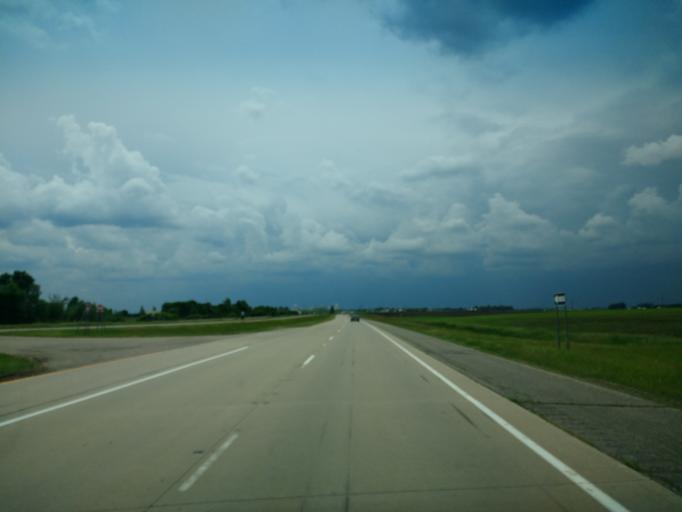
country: US
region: Minnesota
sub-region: Nobles County
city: Worthington
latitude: 43.6515
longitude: -95.5445
